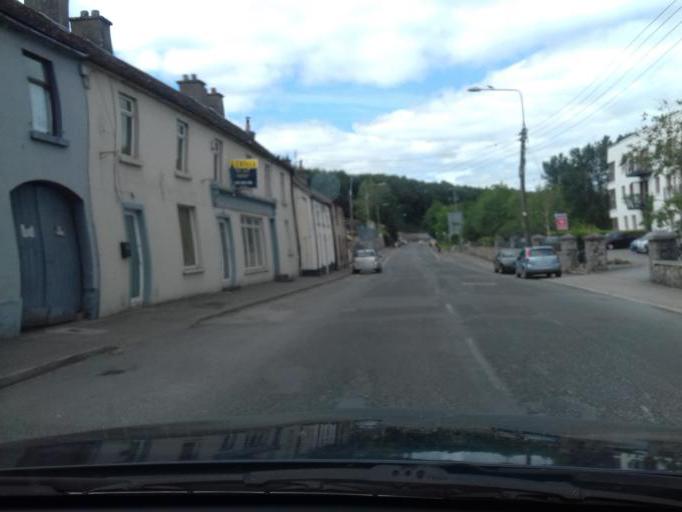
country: IE
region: Leinster
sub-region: Wicklow
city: Baltinglass
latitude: 52.9421
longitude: -6.7117
